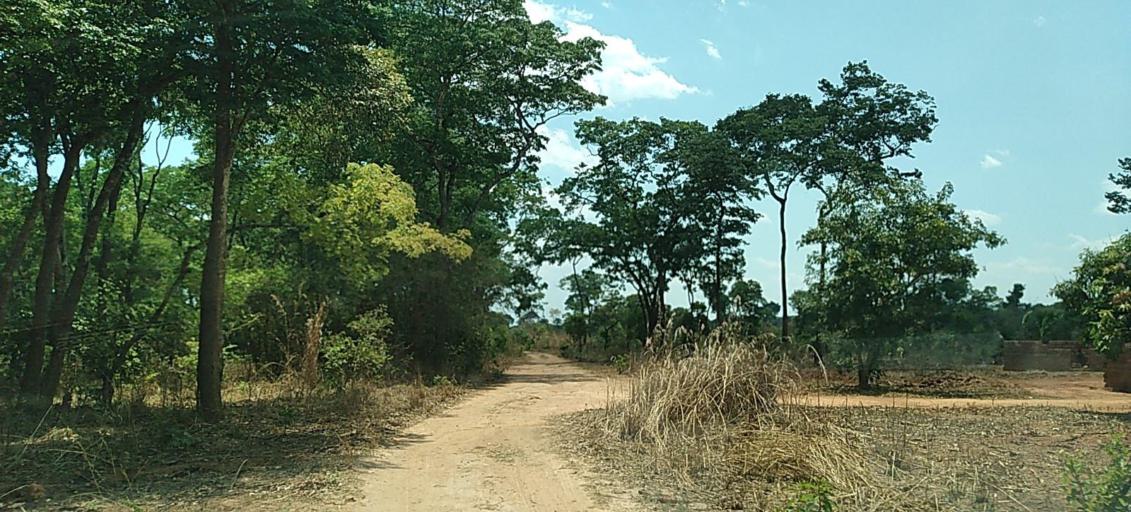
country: ZM
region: Central
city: Kapiri Mposhi
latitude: -13.6313
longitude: 28.7661
